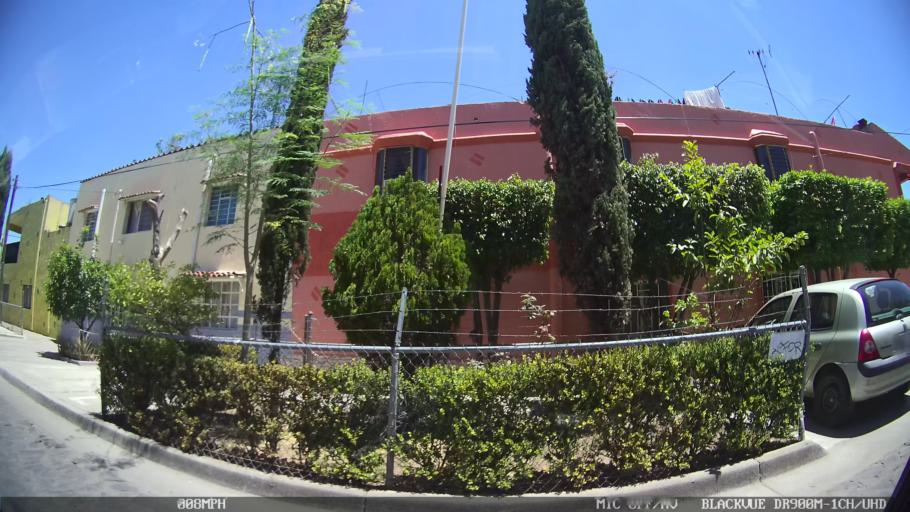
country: MX
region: Jalisco
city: Tlaquepaque
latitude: 20.6571
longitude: -103.2770
